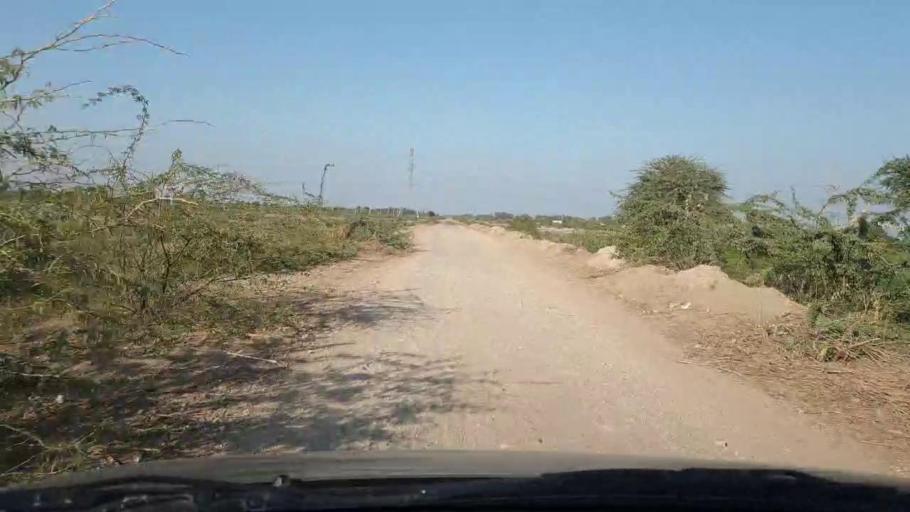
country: PK
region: Sindh
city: Samaro
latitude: 25.1495
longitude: 69.3085
